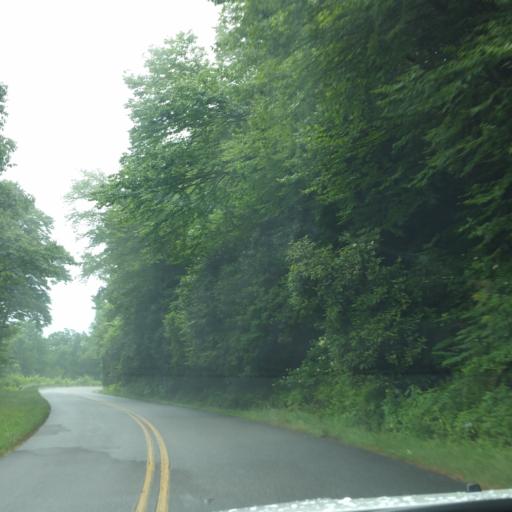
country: US
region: North Carolina
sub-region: Transylvania County
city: Brevard
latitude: 35.3547
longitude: -82.7999
